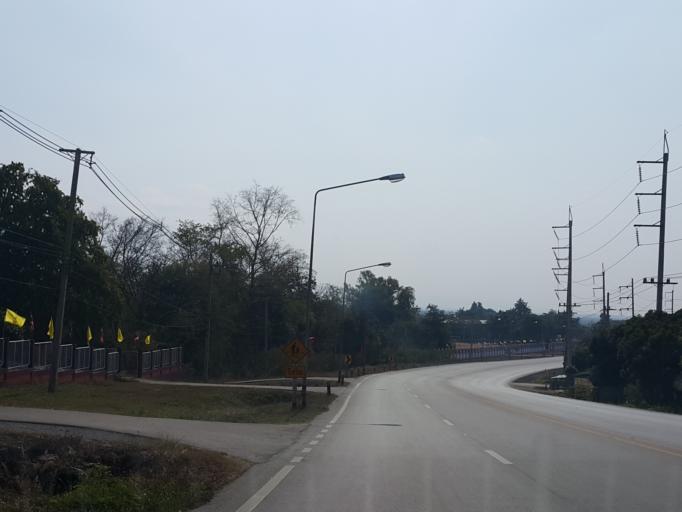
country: TH
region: Chiang Mai
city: Hot
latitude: 18.2985
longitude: 98.6422
